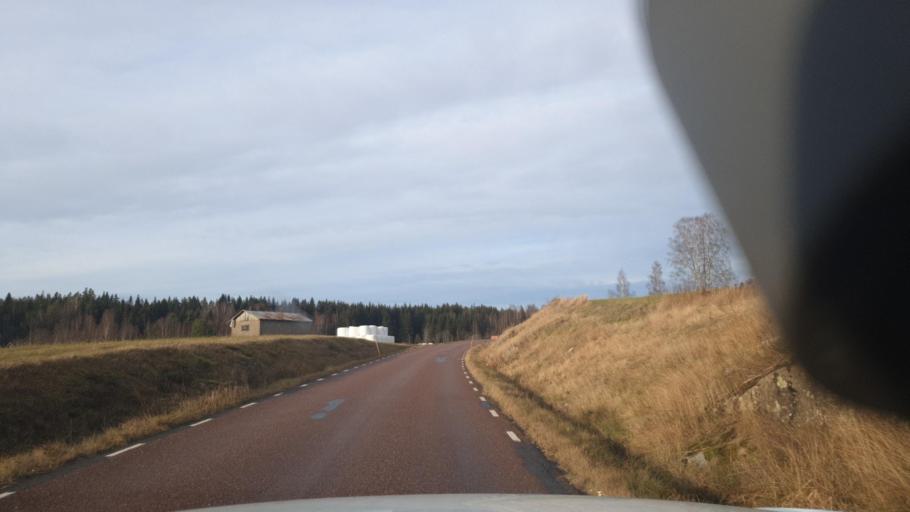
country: NO
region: Ostfold
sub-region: Romskog
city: Romskog
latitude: 59.7113
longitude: 12.0714
